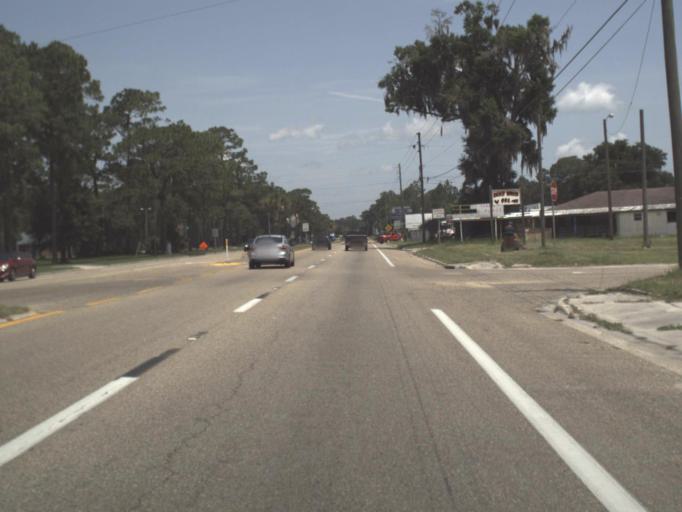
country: US
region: Florida
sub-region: Taylor County
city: Perry
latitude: 30.0763
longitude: -83.5638
